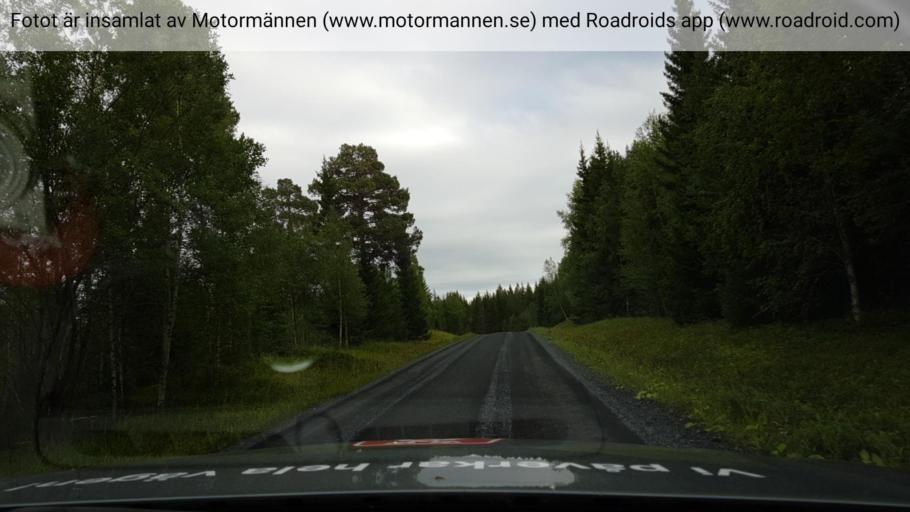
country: SE
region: Jaemtland
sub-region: Krokoms Kommun
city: Valla
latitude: 63.3681
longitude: 13.8859
